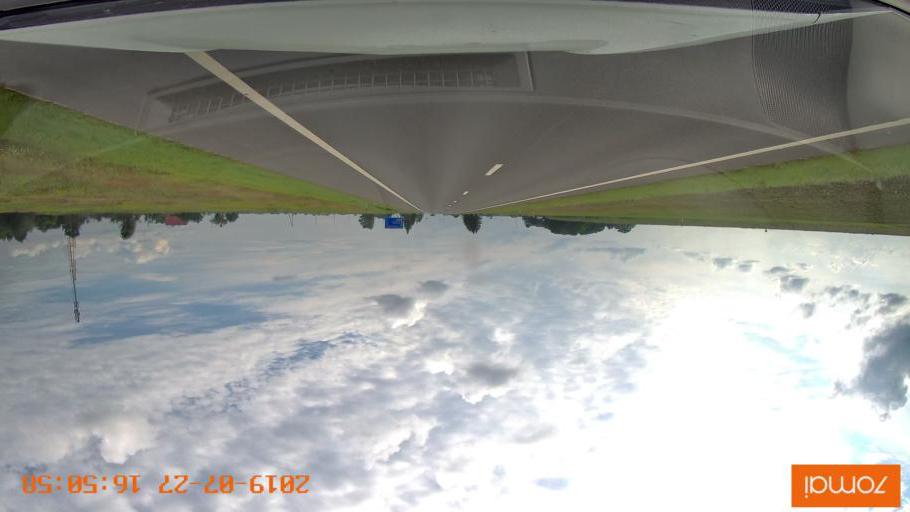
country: RU
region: Kaliningrad
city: Gvardeysk
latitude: 54.6802
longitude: 20.8997
